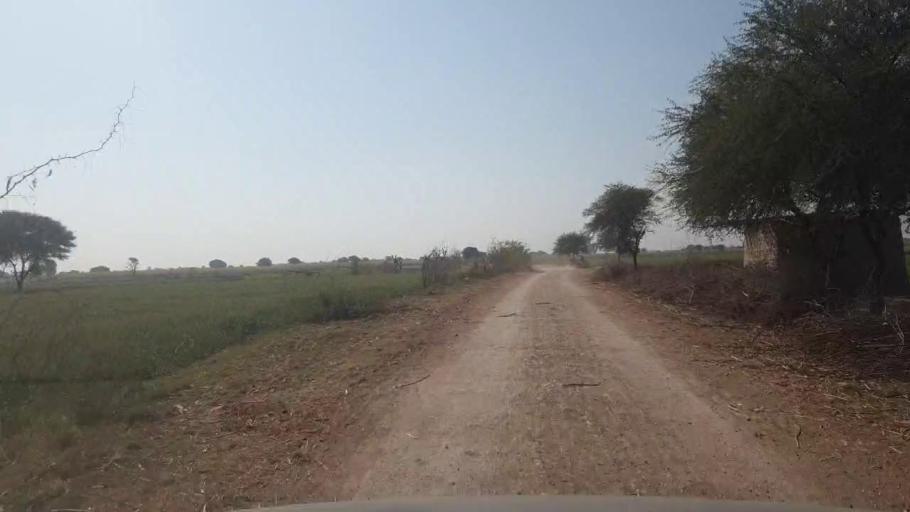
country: PK
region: Sindh
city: Chambar
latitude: 25.3647
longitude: 68.7654
